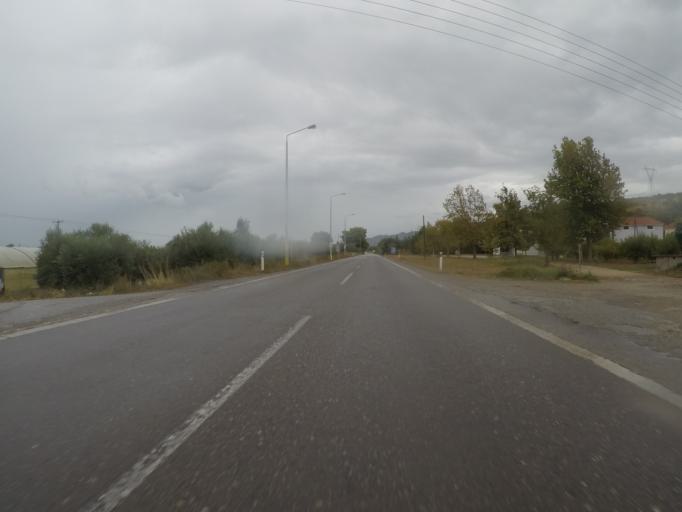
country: GR
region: West Greece
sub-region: Nomos Ileias
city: Zacharo
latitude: 37.4148
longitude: 21.6722
